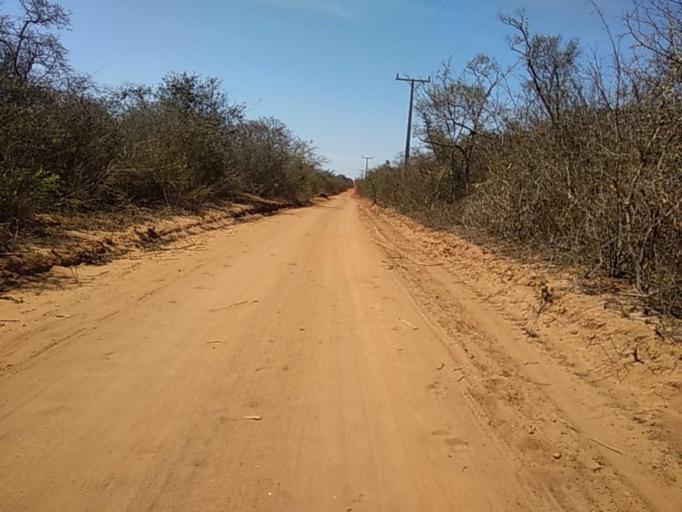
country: BR
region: Bahia
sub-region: Caetite
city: Caetite
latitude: -13.9790
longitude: -42.5121
